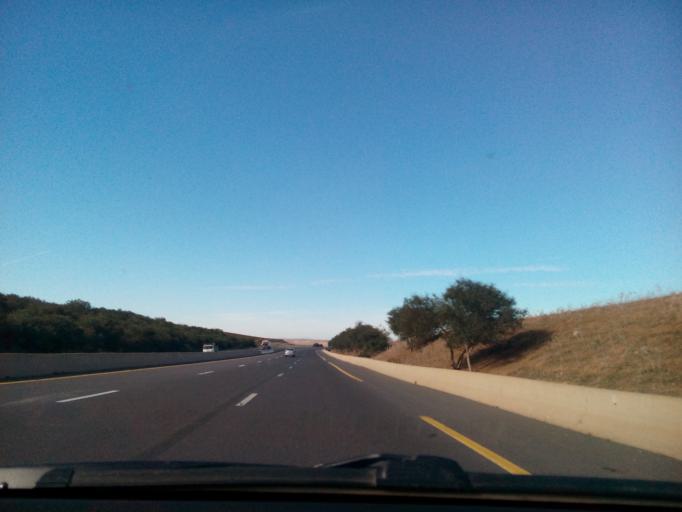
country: DZ
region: Tlemcen
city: Ouled Mimoun
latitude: 35.0311
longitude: -1.0145
